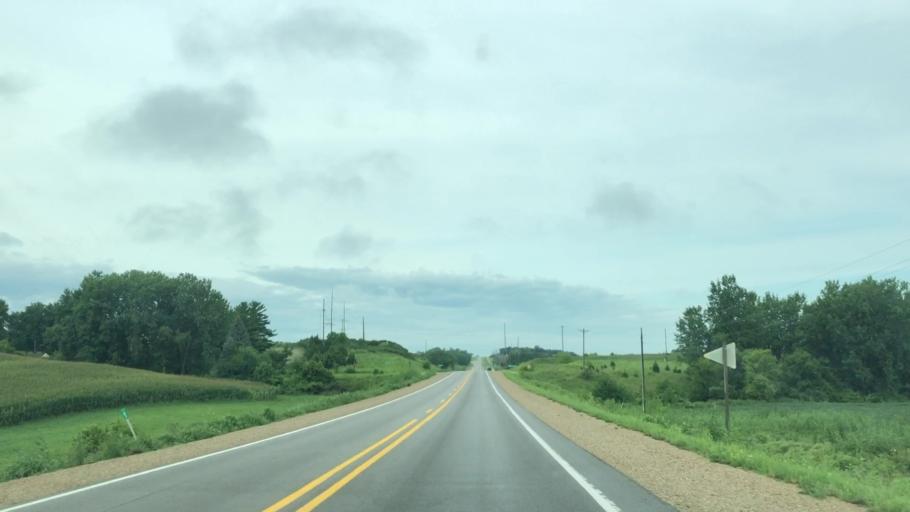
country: US
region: Iowa
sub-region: Marshall County
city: Marshalltown
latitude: 42.0075
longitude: -92.9567
